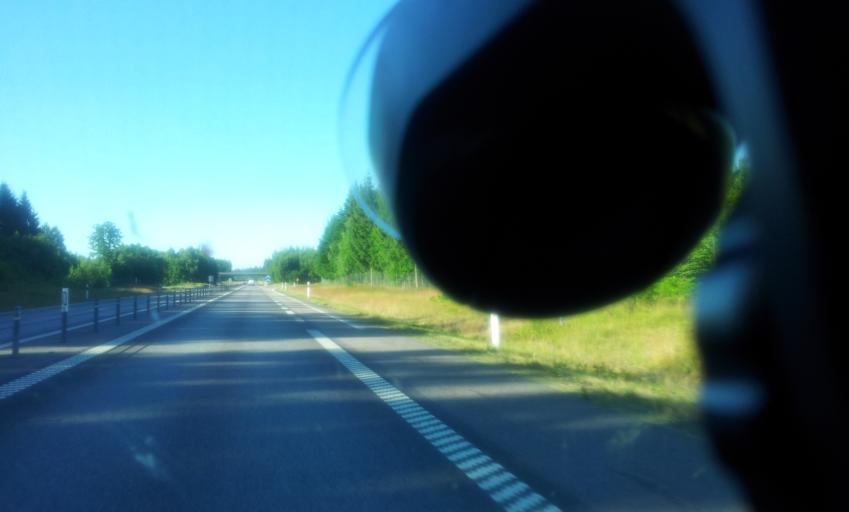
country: SE
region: Kalmar
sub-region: Kalmar Kommun
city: Ljungbyholm
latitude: 56.5561
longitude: 16.0867
